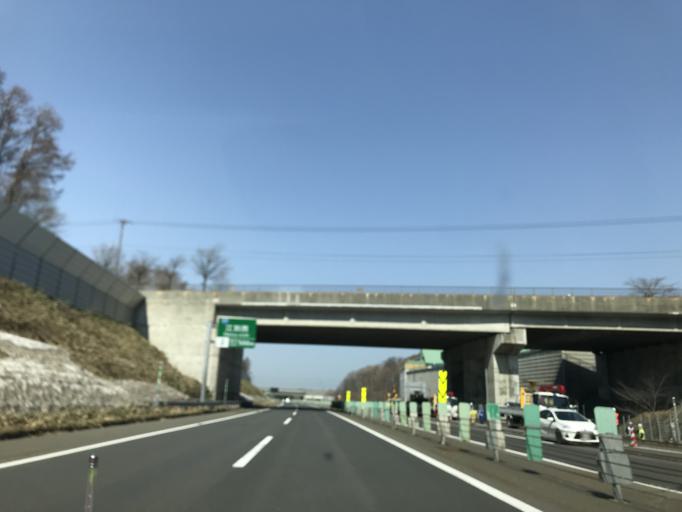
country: JP
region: Hokkaido
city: Ebetsu
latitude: 43.0902
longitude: 141.5078
